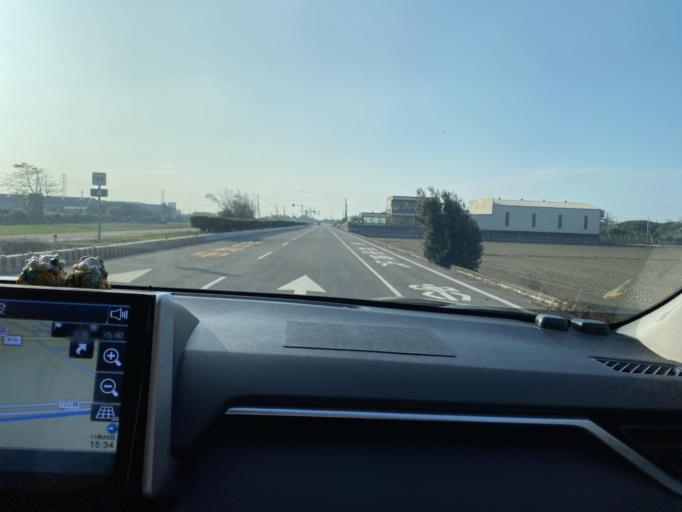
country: TW
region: Taiwan
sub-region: Changhua
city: Chang-hua
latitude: 23.9621
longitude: 120.3774
